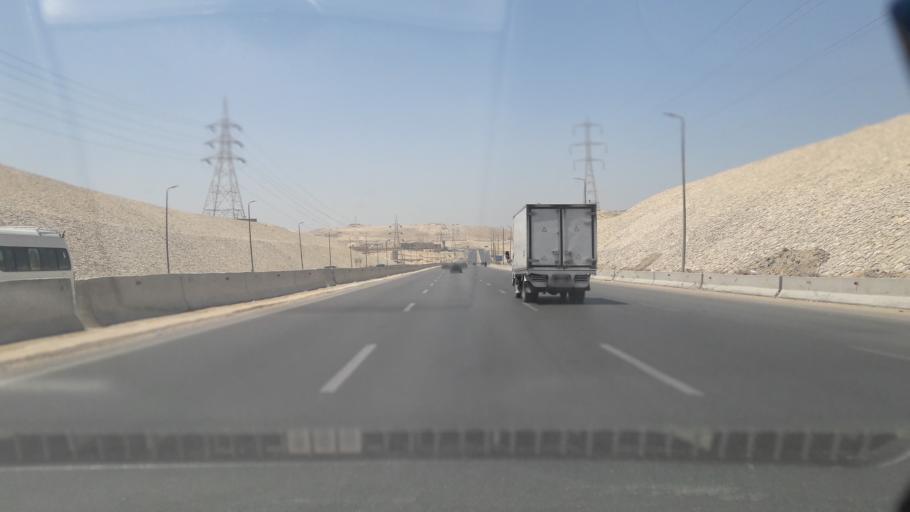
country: EG
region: Al Jizah
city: Awsim
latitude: 30.0114
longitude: 31.0856
